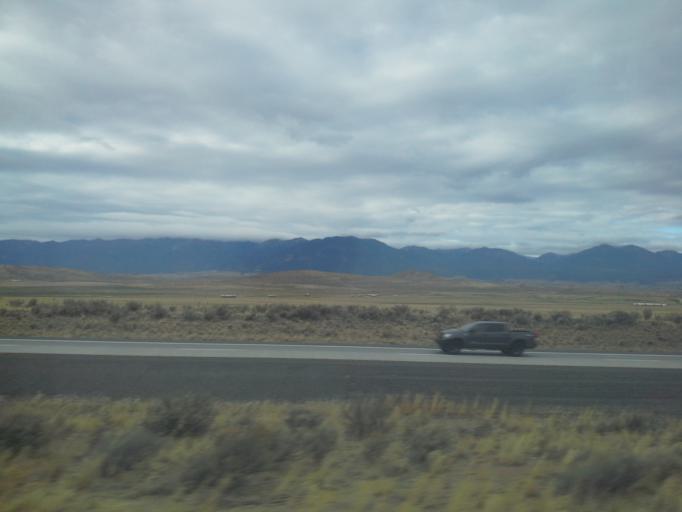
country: US
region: Oregon
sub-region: Baker County
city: Baker City
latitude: 44.9403
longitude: -117.8428
